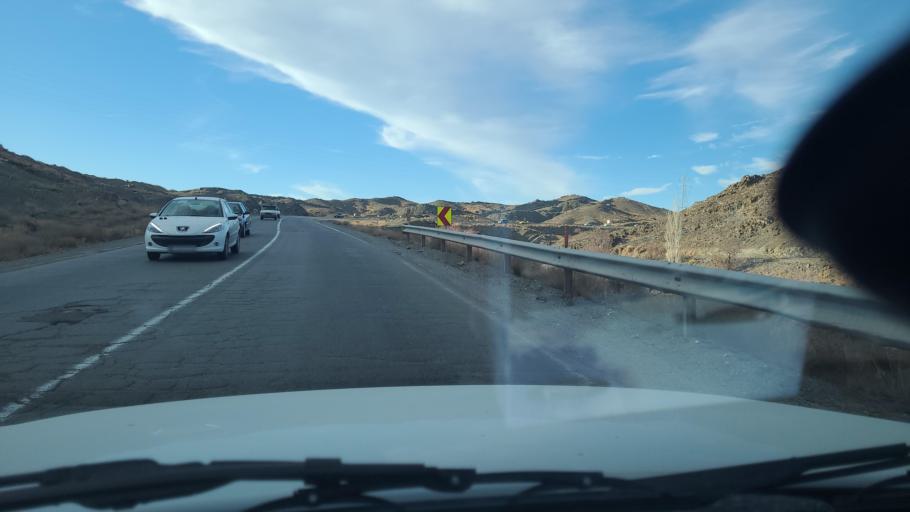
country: IR
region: Razavi Khorasan
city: Sabzevar
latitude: 36.4020
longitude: 57.5500
